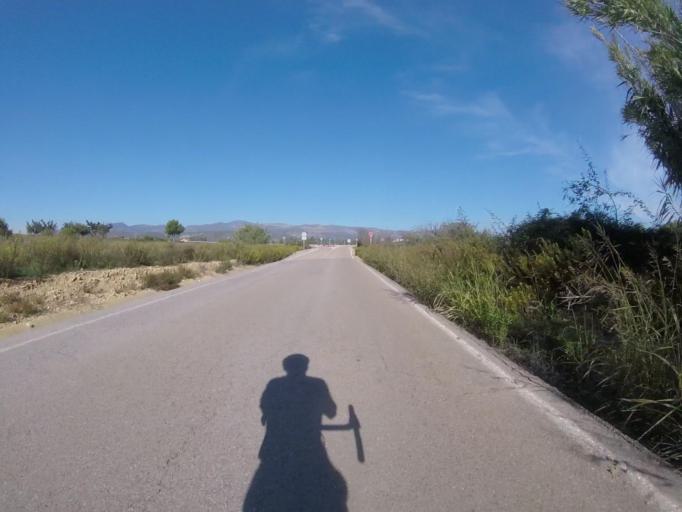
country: ES
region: Valencia
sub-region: Provincia de Castello
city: Benlloch
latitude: 40.2522
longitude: 0.0757
